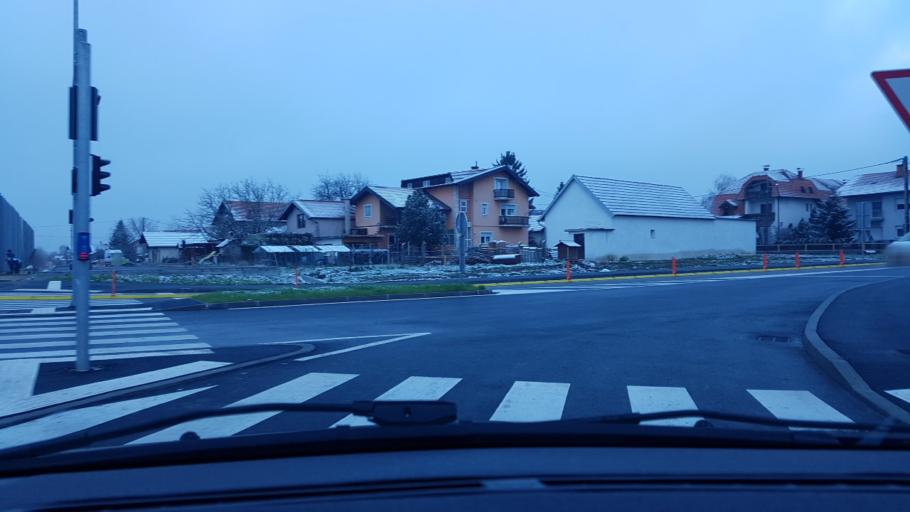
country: HR
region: Zagrebacka
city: Zapresic
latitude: 45.8550
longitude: 15.7961
